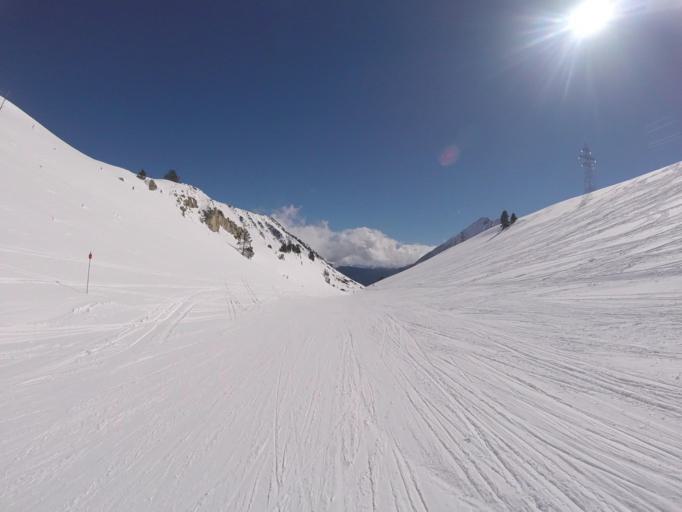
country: ES
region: Catalonia
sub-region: Provincia de Lleida
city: Espot
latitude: 42.6598
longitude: 0.9887
